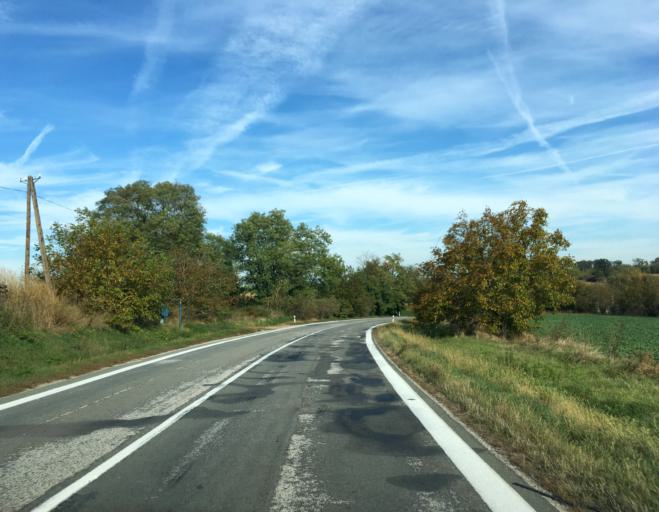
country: SK
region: Nitriansky
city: Svodin
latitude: 48.0290
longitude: 18.4209
